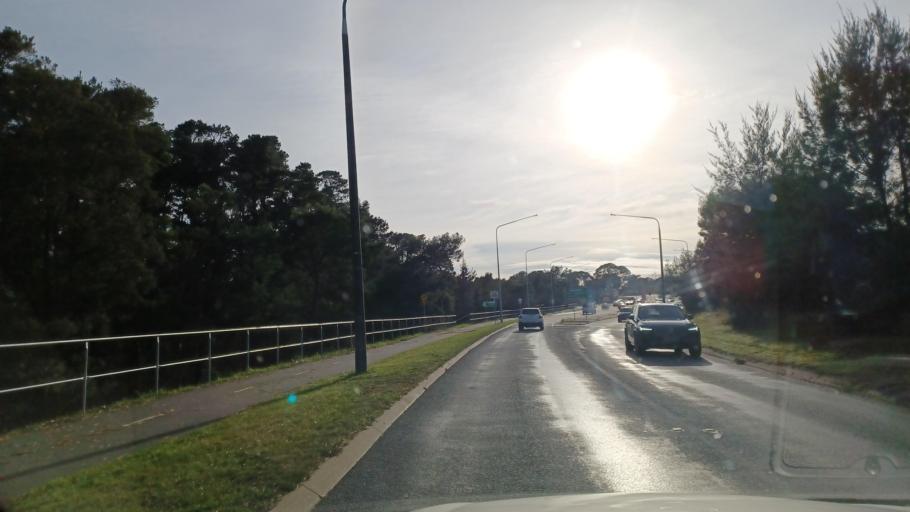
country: AU
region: Australian Capital Territory
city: Belconnen
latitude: -35.1857
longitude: 149.0729
